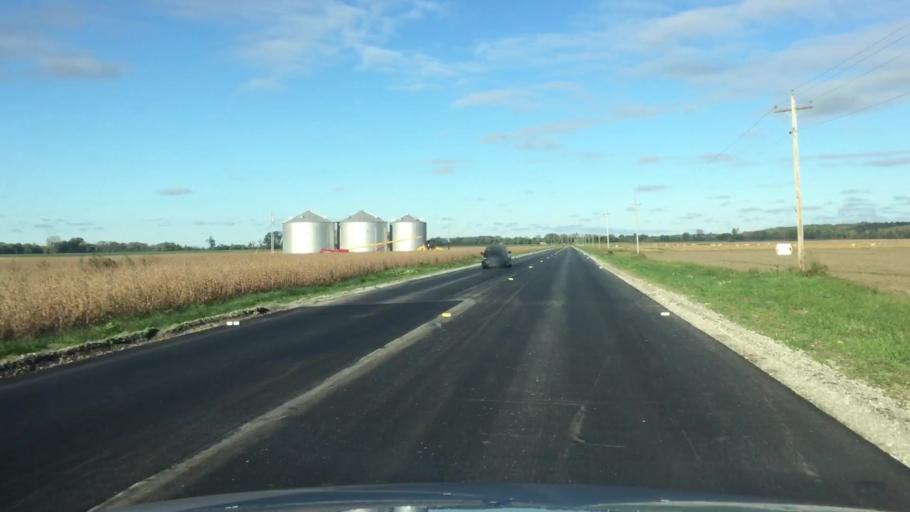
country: US
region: Missouri
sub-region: Howard County
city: New Franklin
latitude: 39.0009
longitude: -92.6808
